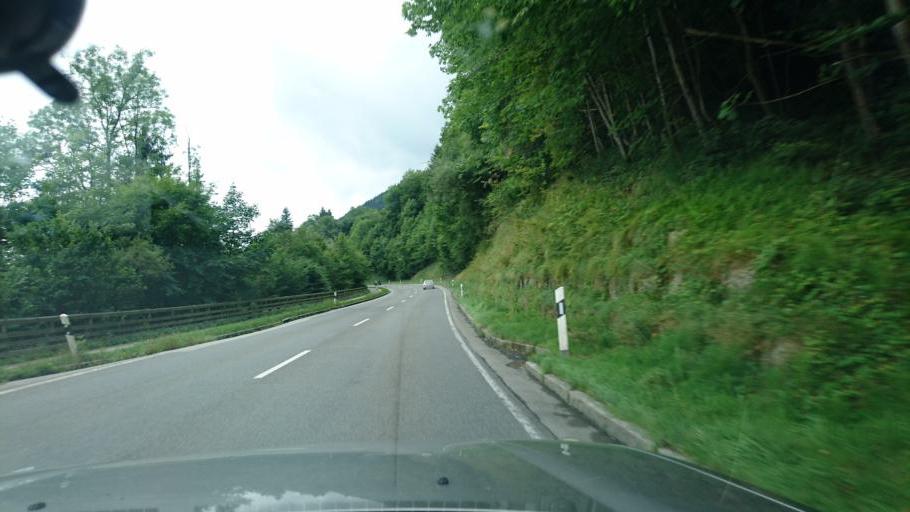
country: DE
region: Bavaria
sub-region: Upper Bavaria
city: Ruhpolding
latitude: 47.7918
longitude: 12.6365
